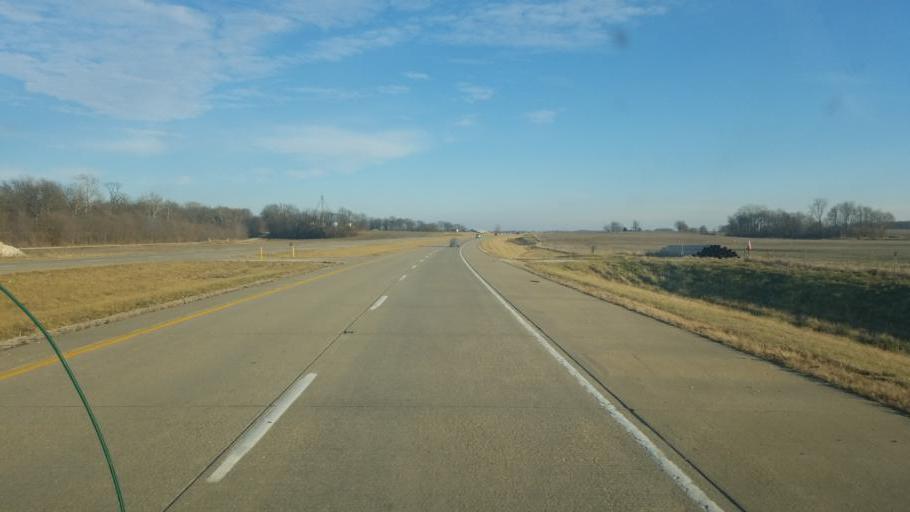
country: US
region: Indiana
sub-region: Knox County
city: Bicknell
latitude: 38.6668
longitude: -87.3290
